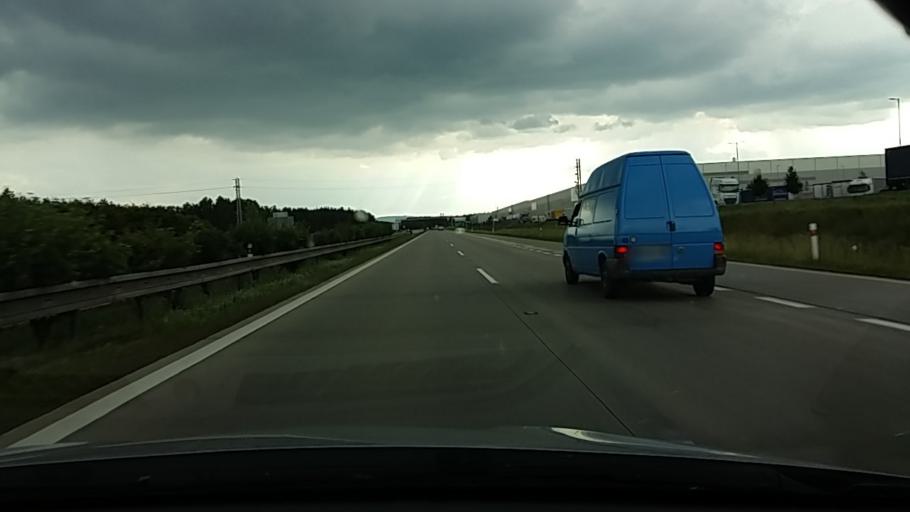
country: CZ
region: Plzensky
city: Bor
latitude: 49.7468
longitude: 12.7773
